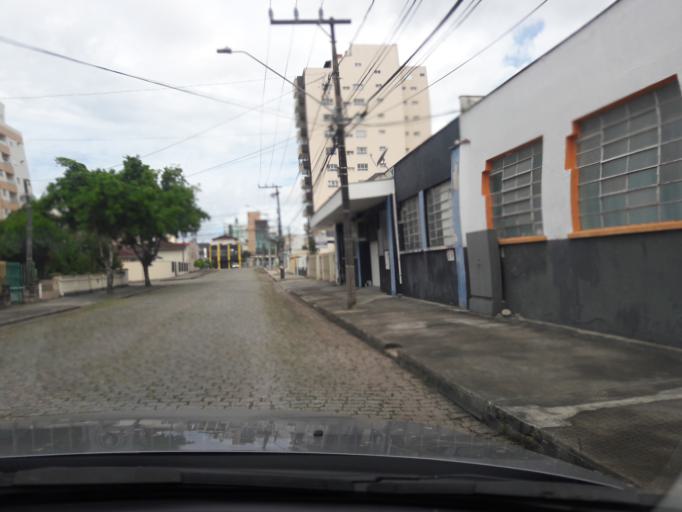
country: BR
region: Santa Catarina
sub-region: Joinville
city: Joinville
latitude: -26.3135
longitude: -48.8472
